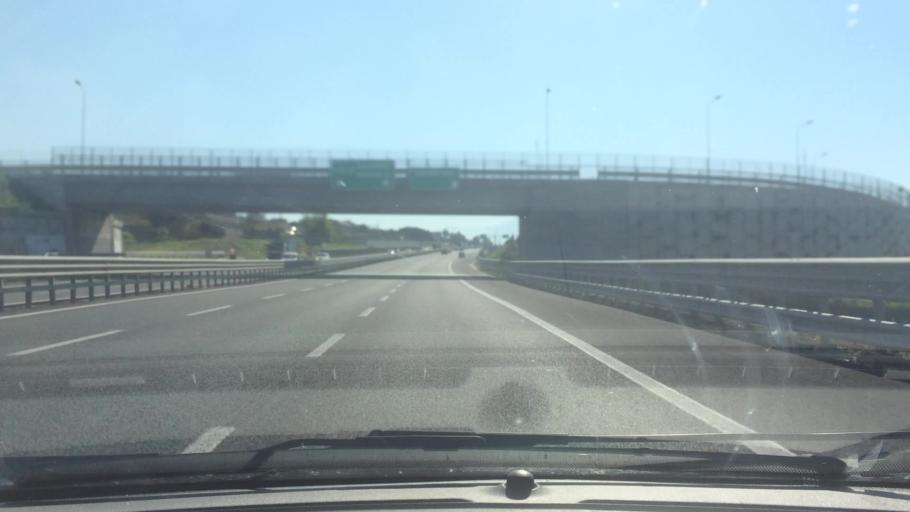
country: IT
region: Campania
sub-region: Provincia di Napoli
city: Ercolano
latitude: 40.8110
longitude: 14.3609
